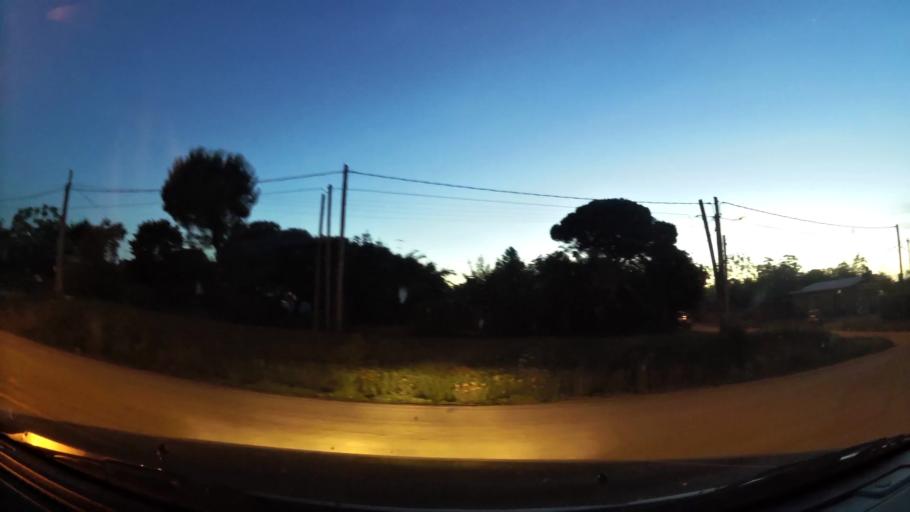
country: UY
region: Canelones
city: Atlantida
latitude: -34.7635
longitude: -55.7592
